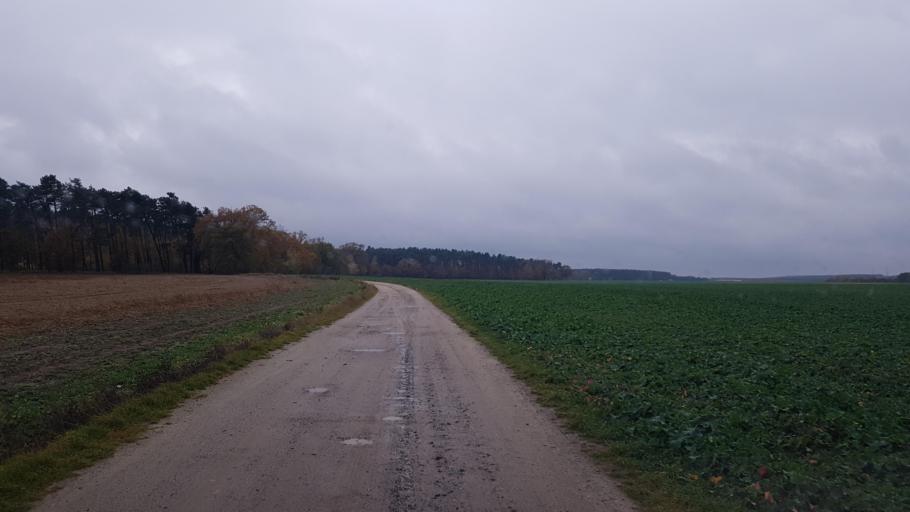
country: DE
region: Brandenburg
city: Drebkau
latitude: 51.6959
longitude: 14.2265
